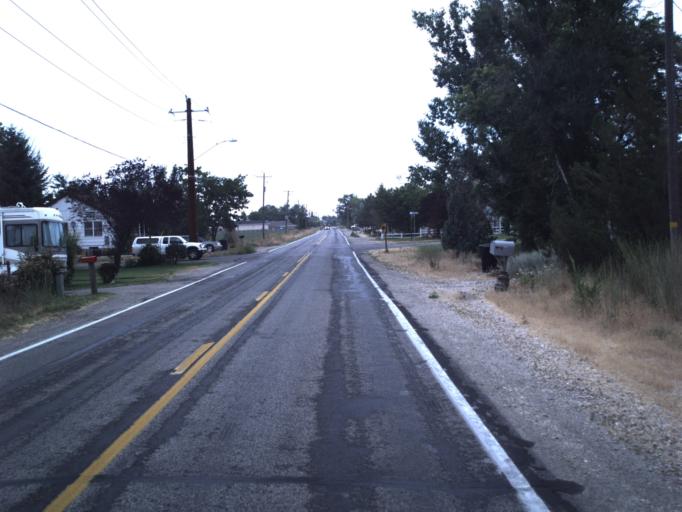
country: US
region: Utah
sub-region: Davis County
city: West Point
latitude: 41.1318
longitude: -112.1126
